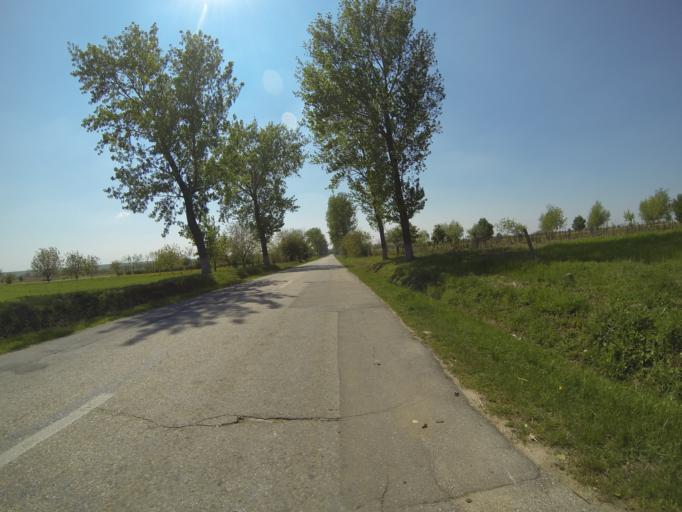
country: RO
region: Dolj
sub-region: Comuna Caraula
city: Caraula
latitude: 44.1974
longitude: 23.2688
